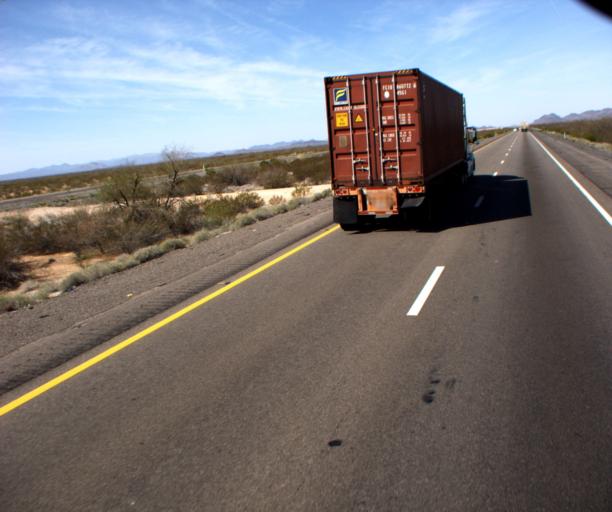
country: US
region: Arizona
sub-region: La Paz County
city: Salome
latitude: 33.5910
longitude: -113.4968
